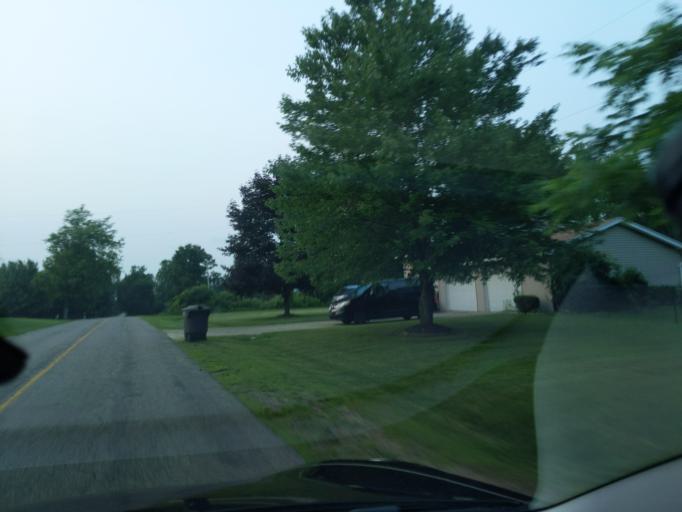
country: US
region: Michigan
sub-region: Jackson County
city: Jackson
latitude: 42.3361
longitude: -84.4334
